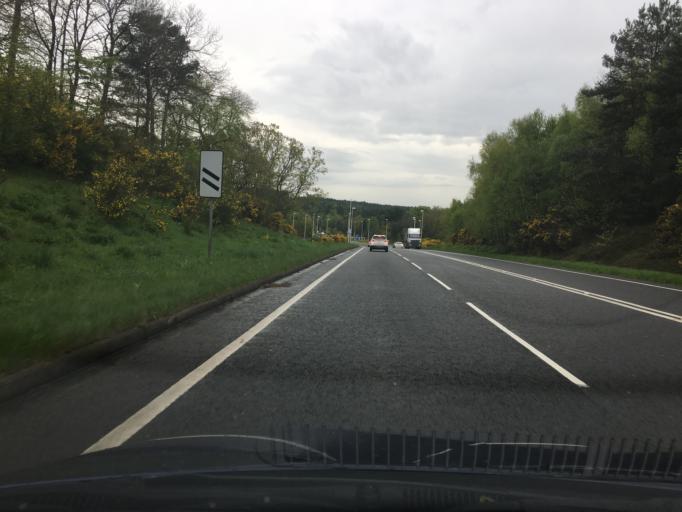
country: GB
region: England
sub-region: Bracknell Forest
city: Crowthorne
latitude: 51.3657
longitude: -0.7669
